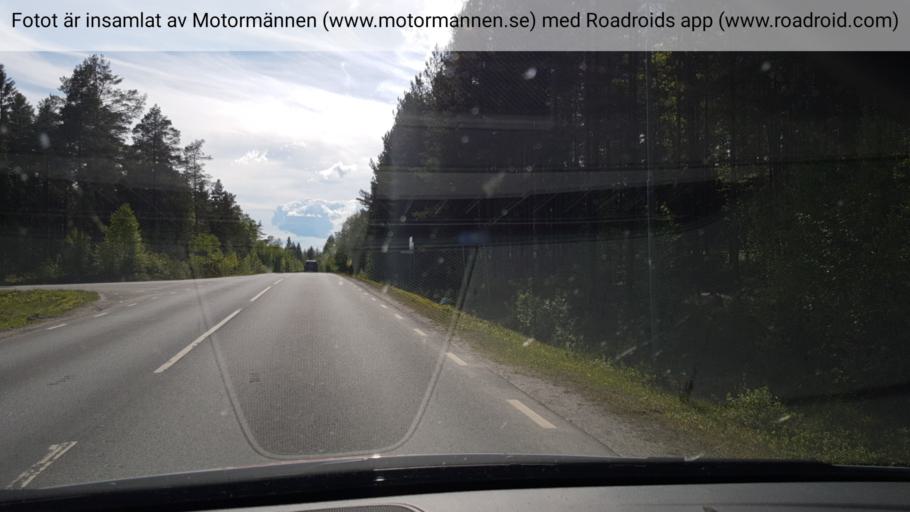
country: SE
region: Vaesterbotten
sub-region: Umea Kommun
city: Saevar
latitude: 63.8967
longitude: 20.5370
